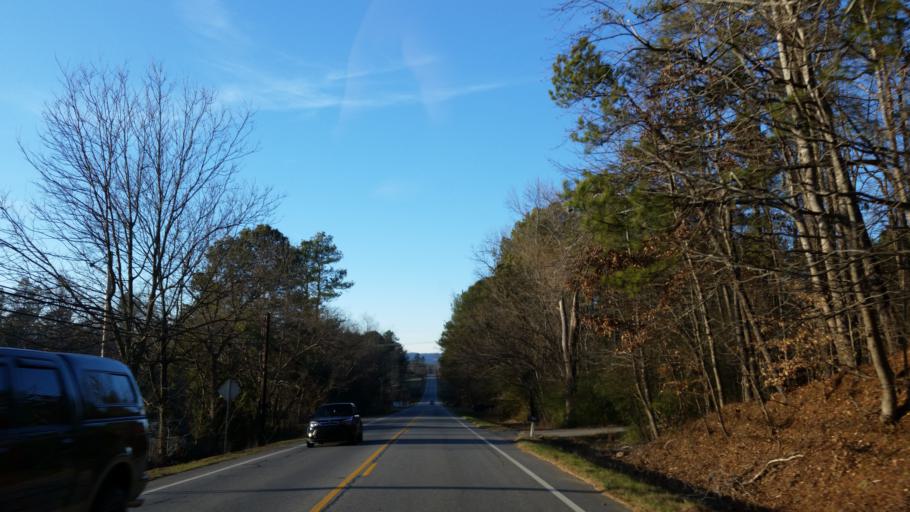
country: US
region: Georgia
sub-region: Gordon County
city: Calhoun
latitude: 34.6349
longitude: -84.9619
